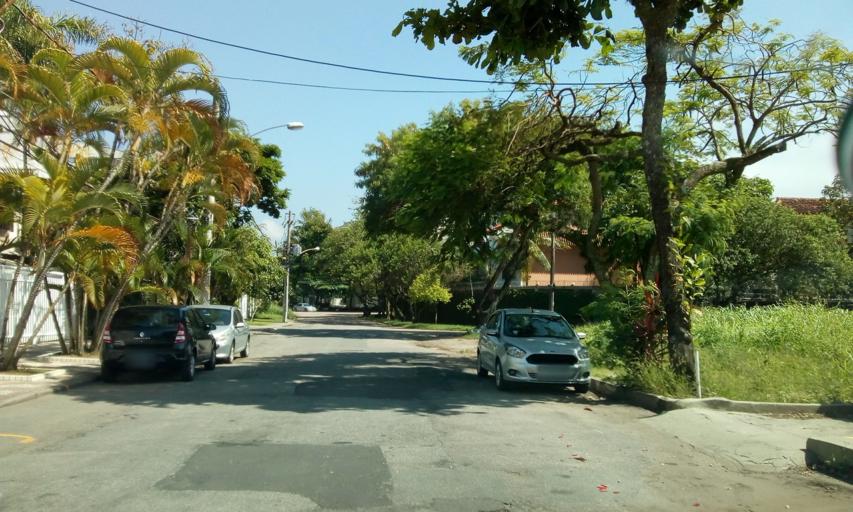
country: BR
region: Rio de Janeiro
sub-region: Nilopolis
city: Nilopolis
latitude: -23.0171
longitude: -43.4619
